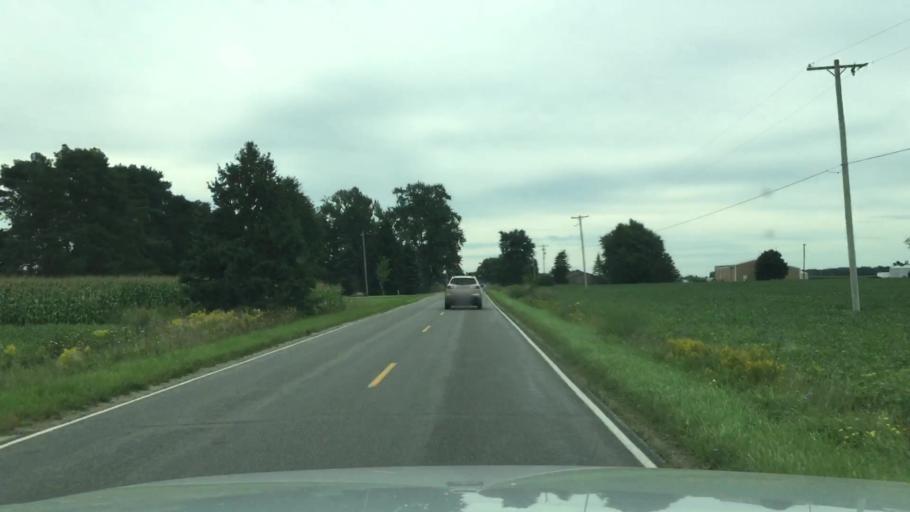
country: US
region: Michigan
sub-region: Shiawassee County
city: Durand
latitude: 43.0232
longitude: -83.9871
